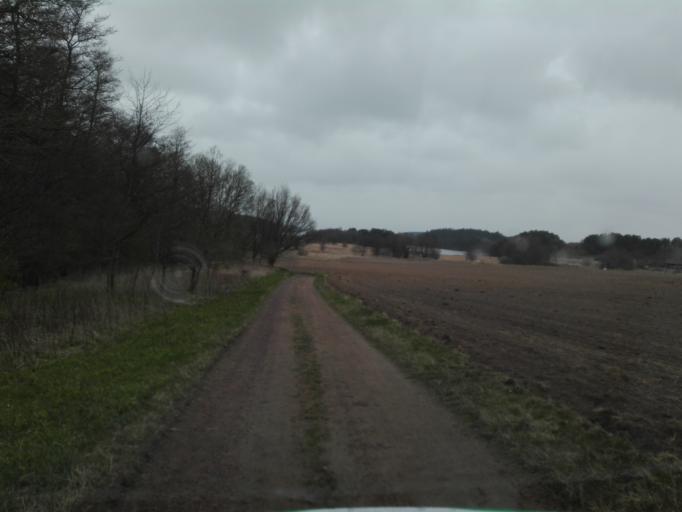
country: SE
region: OEstergoetland
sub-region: Linkopings Kommun
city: Sturefors
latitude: 58.2947
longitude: 15.8631
